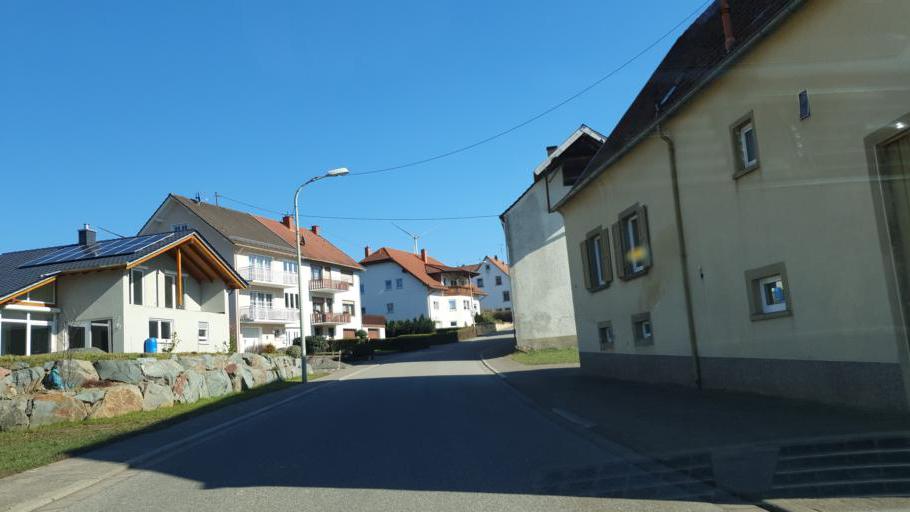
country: DE
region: Rheinland-Pfalz
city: Schellweiler
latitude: 49.5154
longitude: 7.3903
